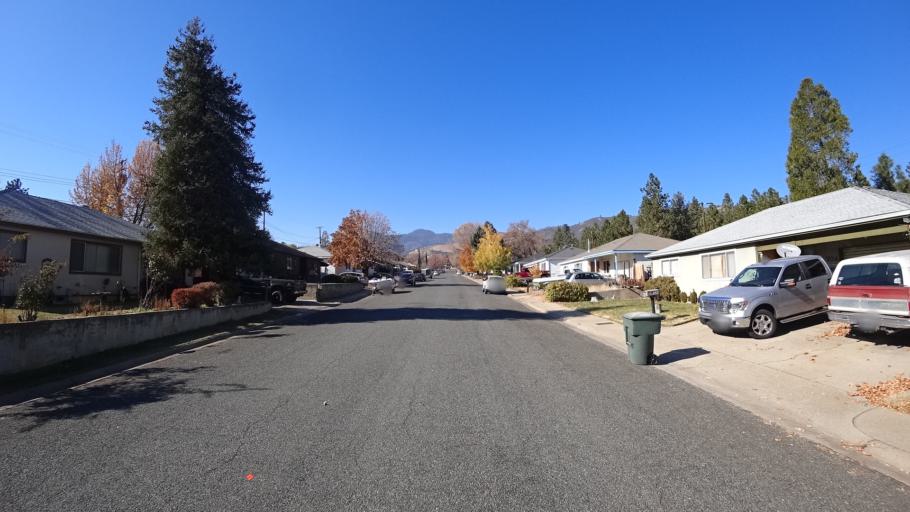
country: US
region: California
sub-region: Siskiyou County
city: Yreka
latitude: 41.7403
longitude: -122.6408
